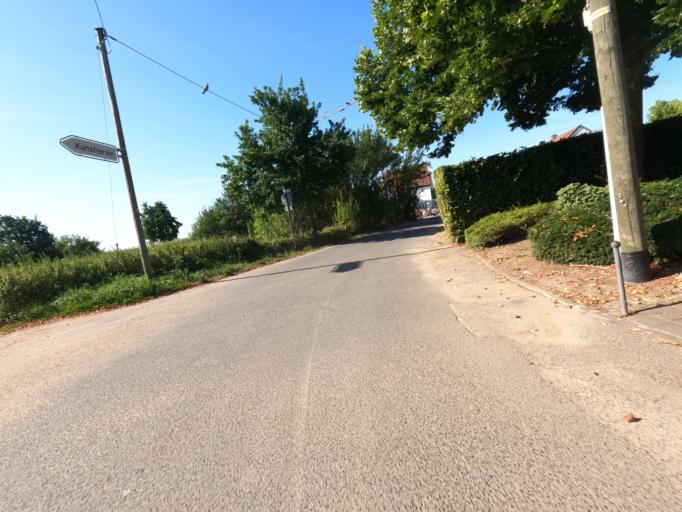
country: DE
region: North Rhine-Westphalia
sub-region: Regierungsbezirk Koln
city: Heinsberg
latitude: 51.0787
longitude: 6.1279
